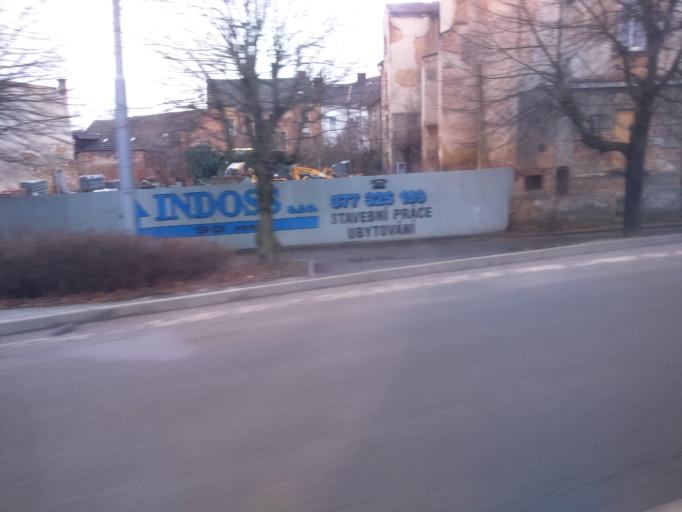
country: CZ
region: Plzensky
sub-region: Okres Plzen-Mesto
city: Pilsen
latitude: 49.7422
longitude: 13.3466
